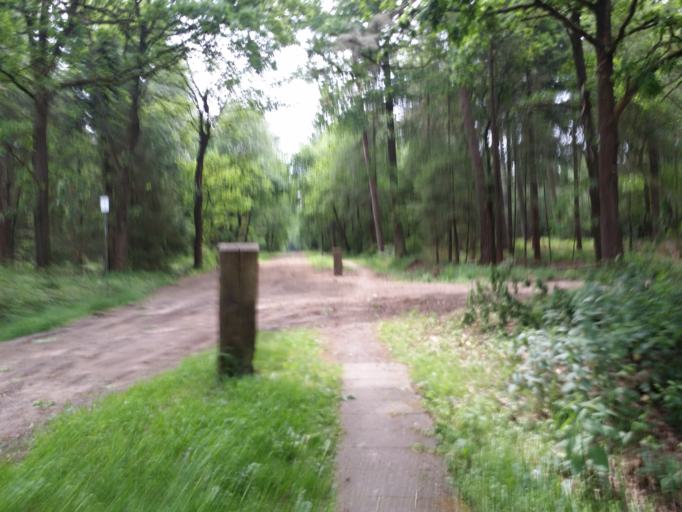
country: DE
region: Lower Saxony
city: Friedeburg
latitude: 53.4969
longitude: 7.8145
